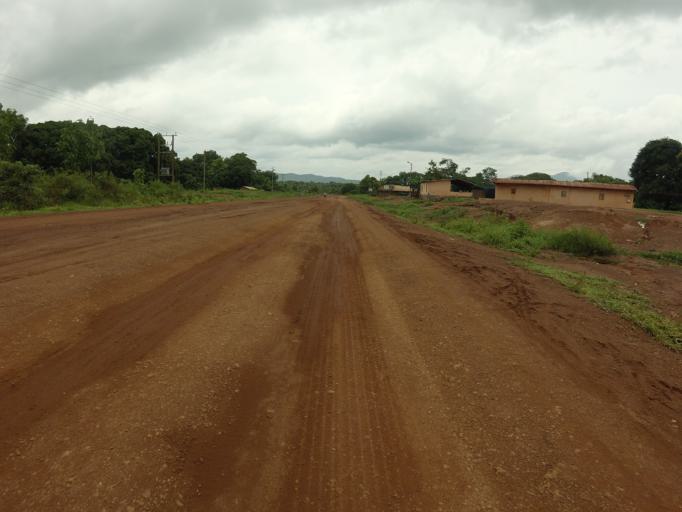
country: GH
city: Kpandae
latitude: 8.3003
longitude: 0.4863
